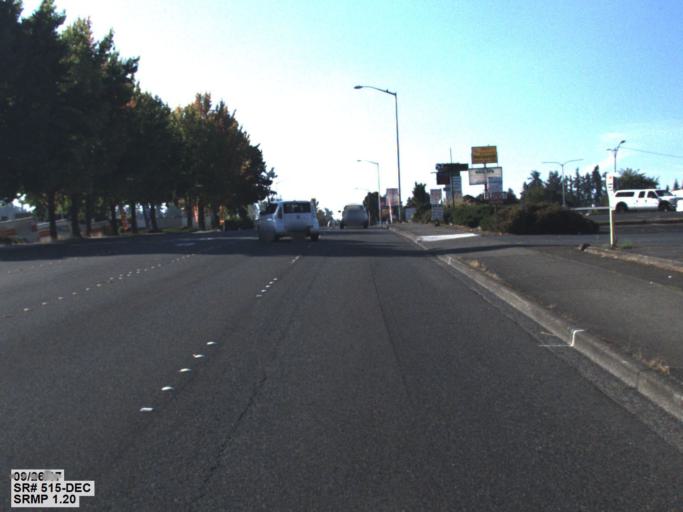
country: US
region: Washington
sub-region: King County
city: Kent
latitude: 47.3899
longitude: -122.2022
